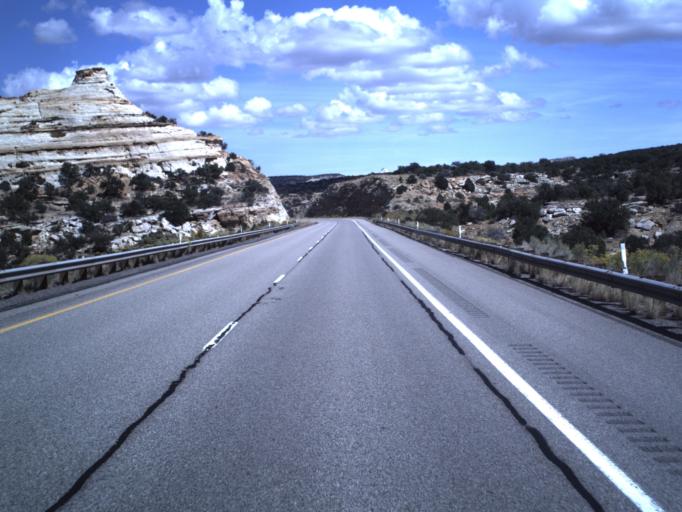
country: US
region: Utah
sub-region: Emery County
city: Ferron
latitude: 38.8522
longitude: -110.8792
